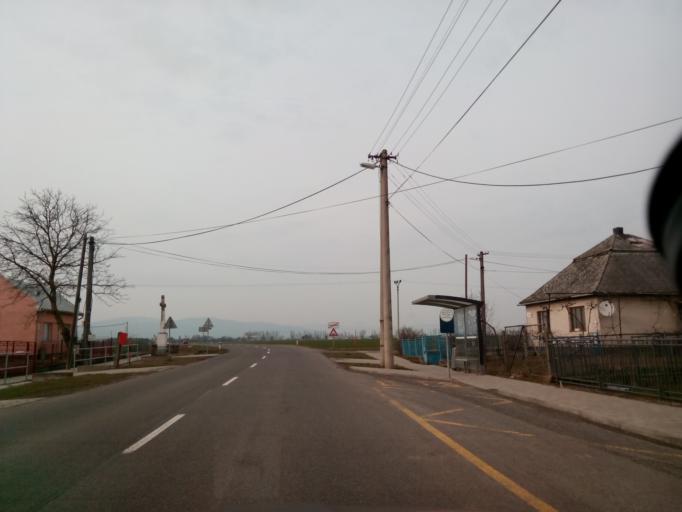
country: SK
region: Kosicky
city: Trebisov
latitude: 48.5882
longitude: 21.6405
